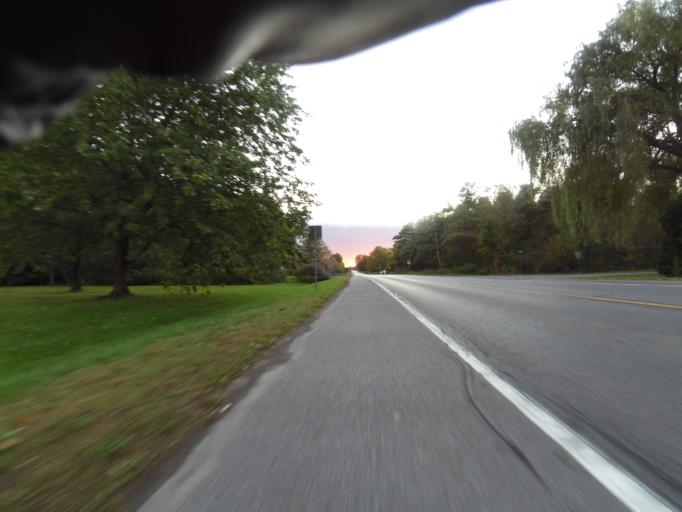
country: CA
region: Ontario
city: Quinte West
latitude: 44.0409
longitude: -77.6764
